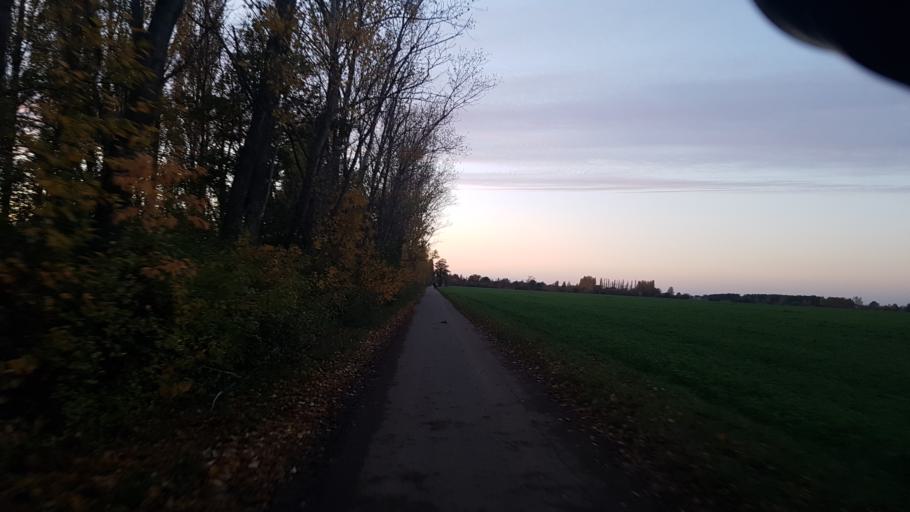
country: DE
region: Brandenburg
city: Bad Liebenwerda
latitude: 51.5098
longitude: 13.3149
